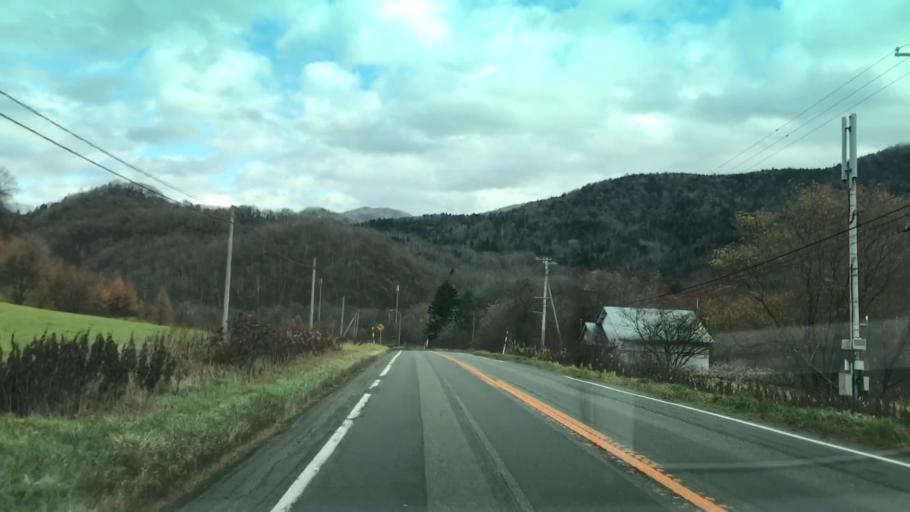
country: JP
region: Hokkaido
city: Shizunai-furukawacho
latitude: 42.8121
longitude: 142.4153
